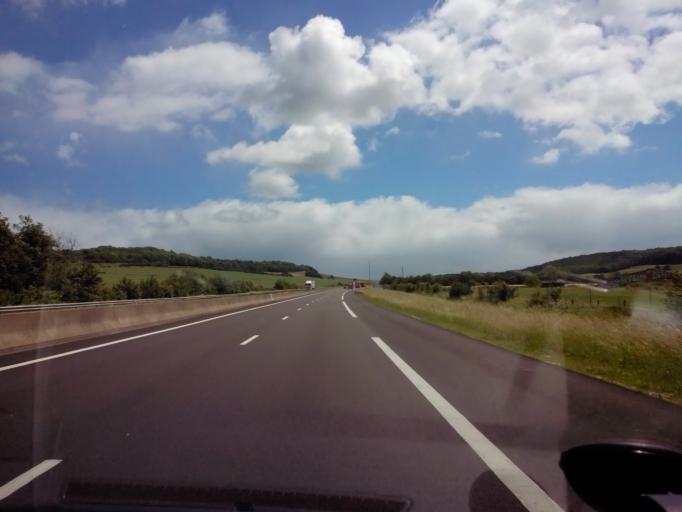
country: FR
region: Champagne-Ardenne
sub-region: Departement de la Haute-Marne
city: Nogent-le-Bas
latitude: 47.9578
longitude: 5.4049
